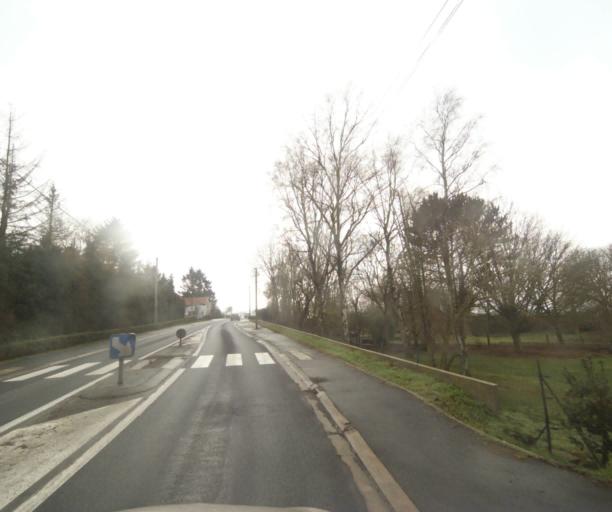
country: FR
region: Nord-Pas-de-Calais
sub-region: Departement du Nord
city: Vendegies-sur-Ecaillon
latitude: 50.2804
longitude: 3.5156
